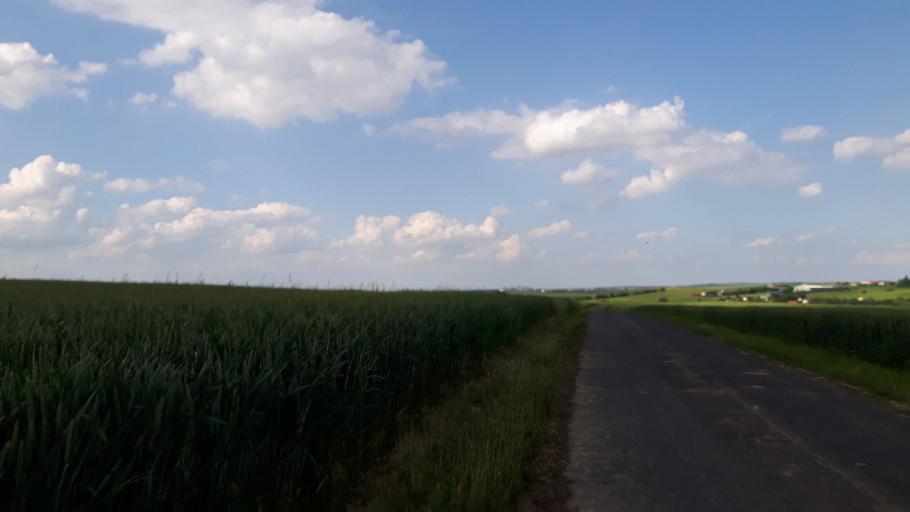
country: DE
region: Bavaria
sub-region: Regierungsbezirk Unterfranken
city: Geroldshausen
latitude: 49.7019
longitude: 9.9190
